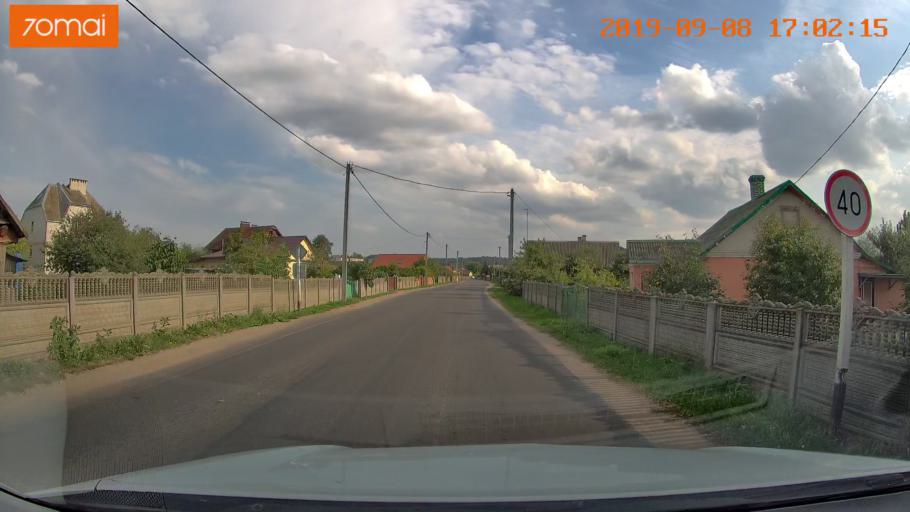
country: BY
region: Grodnenskaya
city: Hrodna
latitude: 53.7049
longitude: 23.9381
